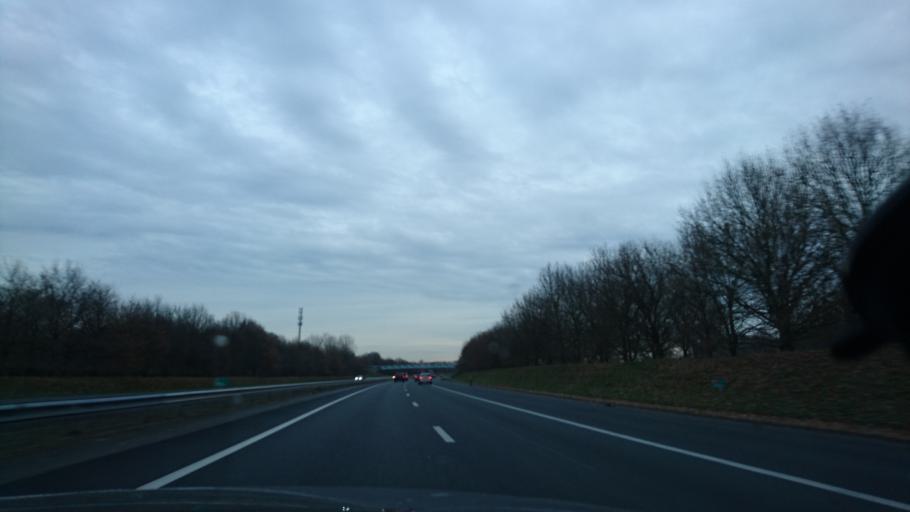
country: NL
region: Overijssel
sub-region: Gemeente Hengelo
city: Hengelo
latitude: 52.2880
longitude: 6.7932
